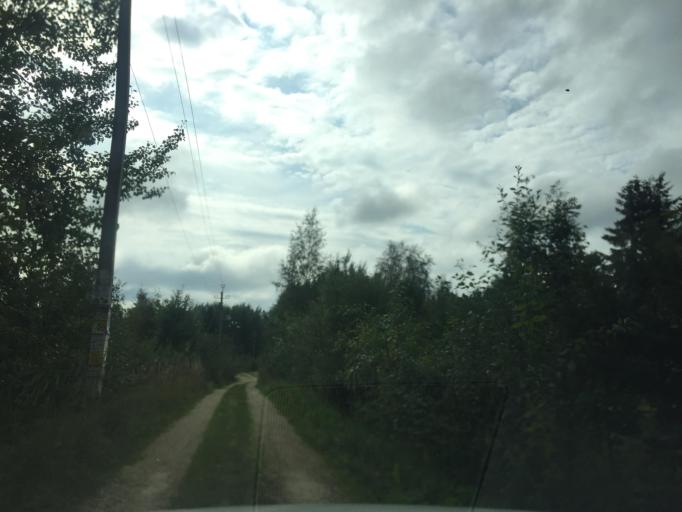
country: RU
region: Leningrad
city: Rozhdestveno
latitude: 59.2962
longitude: 30.0130
